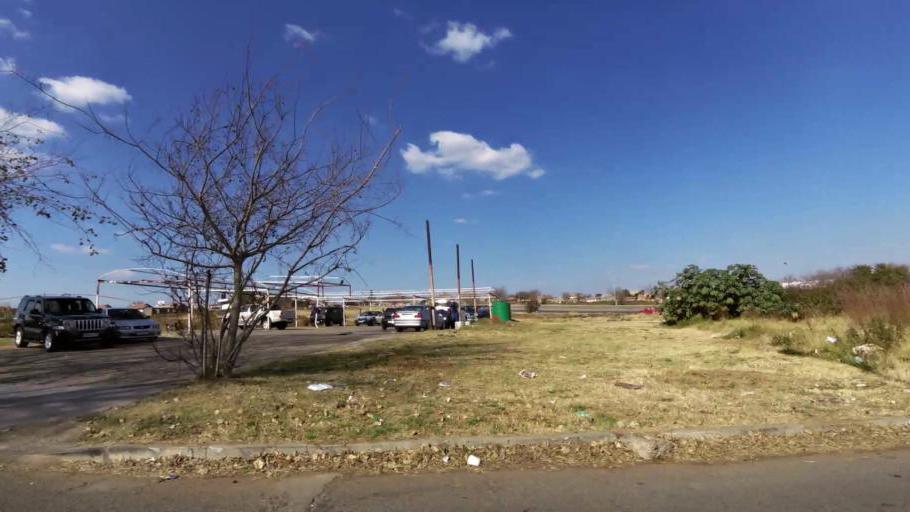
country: ZA
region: Gauteng
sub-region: City of Johannesburg Metropolitan Municipality
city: Roodepoort
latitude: -26.2137
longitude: 27.8840
